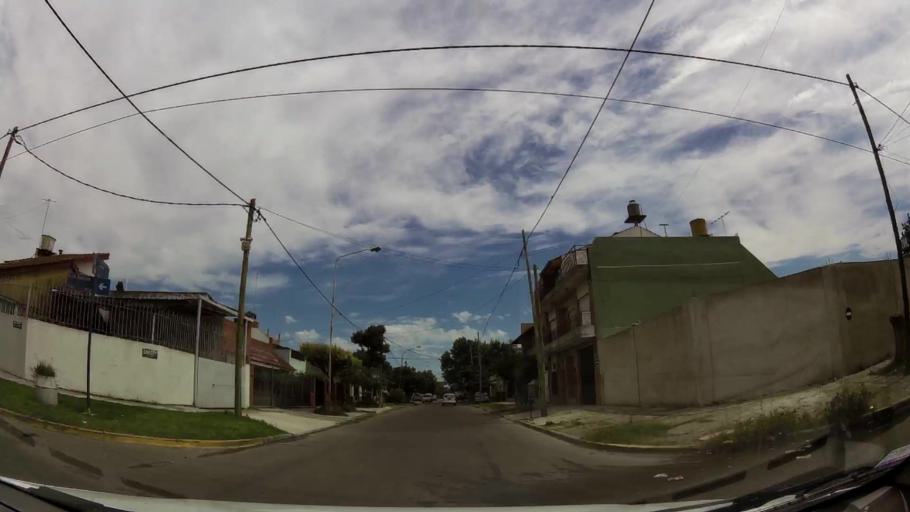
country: AR
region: Buenos Aires
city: San Justo
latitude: -34.6824
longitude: -58.5374
